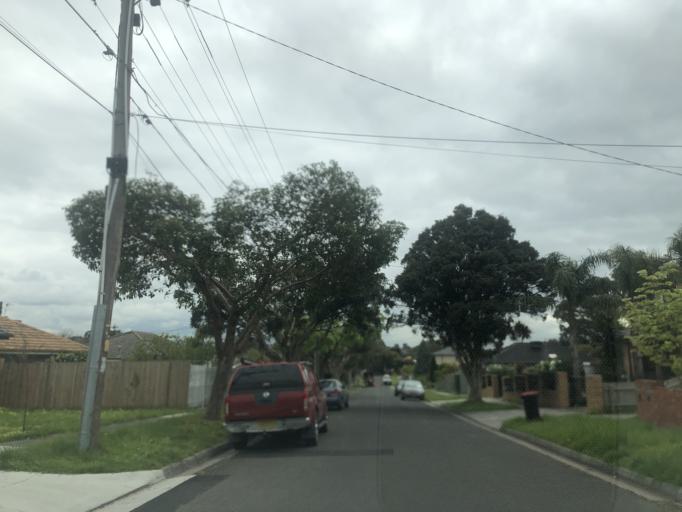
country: AU
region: Victoria
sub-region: Greater Dandenong
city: Dandenong North
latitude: -37.9670
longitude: 145.1995
